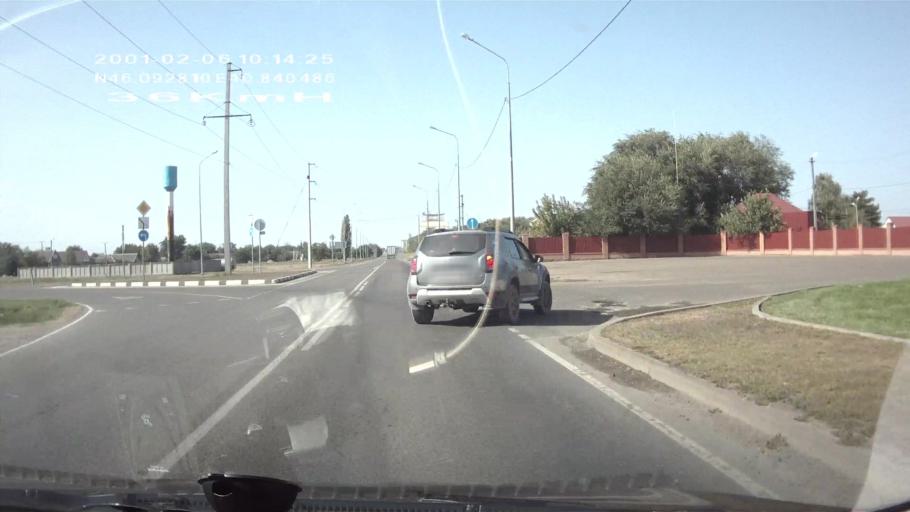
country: RU
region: Krasnodarskiy
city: Belaya Glina
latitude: 46.0928
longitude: 40.8404
